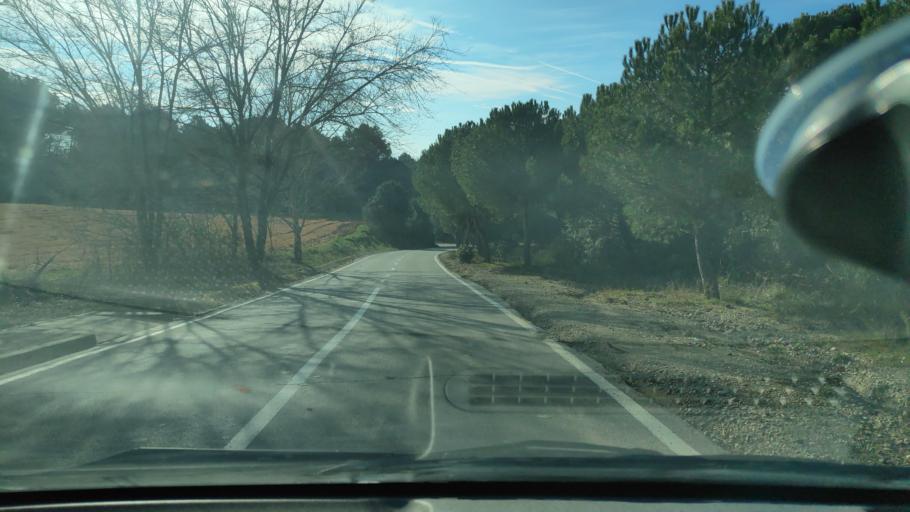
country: ES
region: Catalonia
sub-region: Provincia de Barcelona
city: Rubi
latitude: 41.4980
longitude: 2.0614
